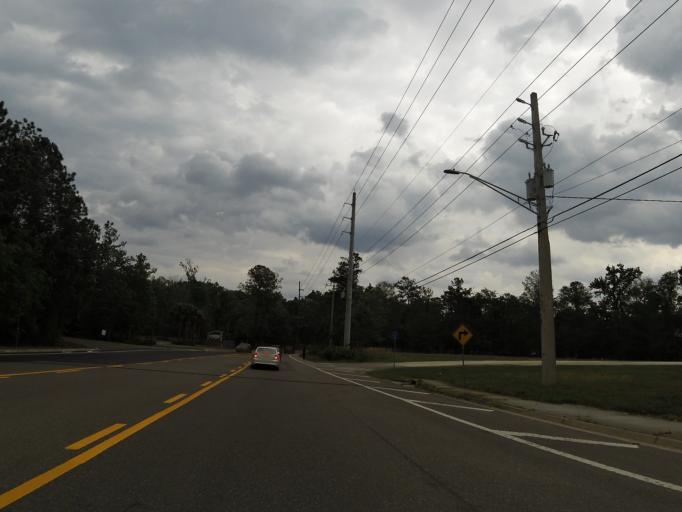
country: US
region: Florida
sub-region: Clay County
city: Bellair-Meadowbrook Terrace
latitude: 30.2043
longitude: -81.7379
